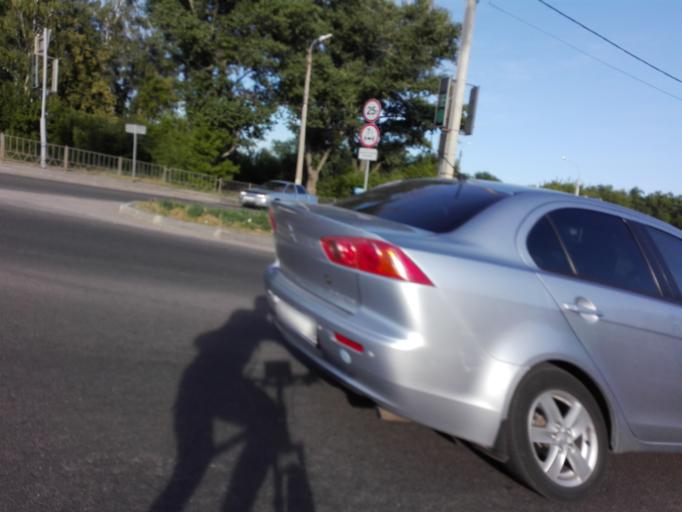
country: RU
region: Orjol
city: Orel
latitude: 52.9629
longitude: 36.0337
